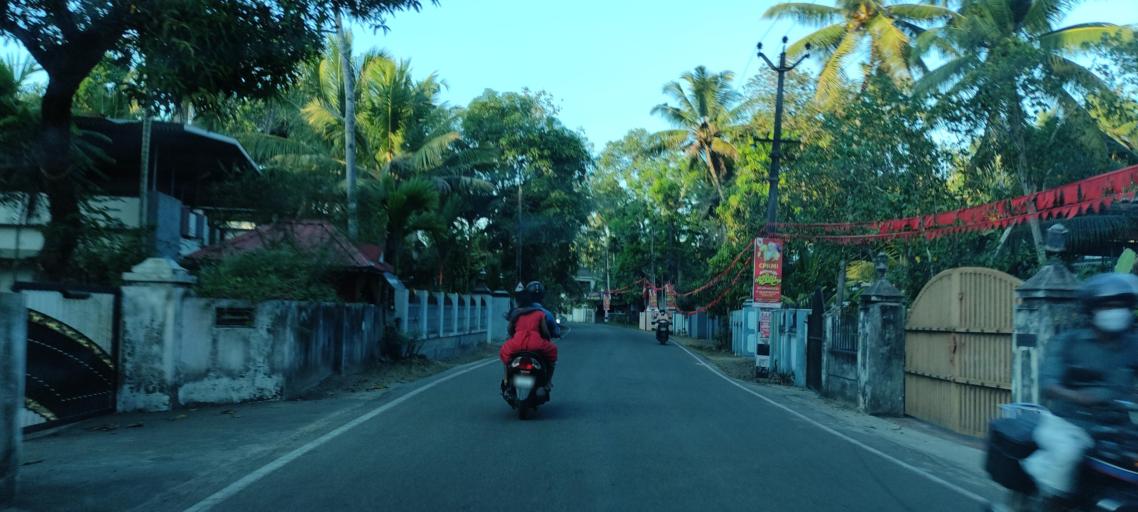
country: IN
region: Kerala
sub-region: Alappuzha
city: Kayankulam
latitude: 9.1851
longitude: 76.4719
